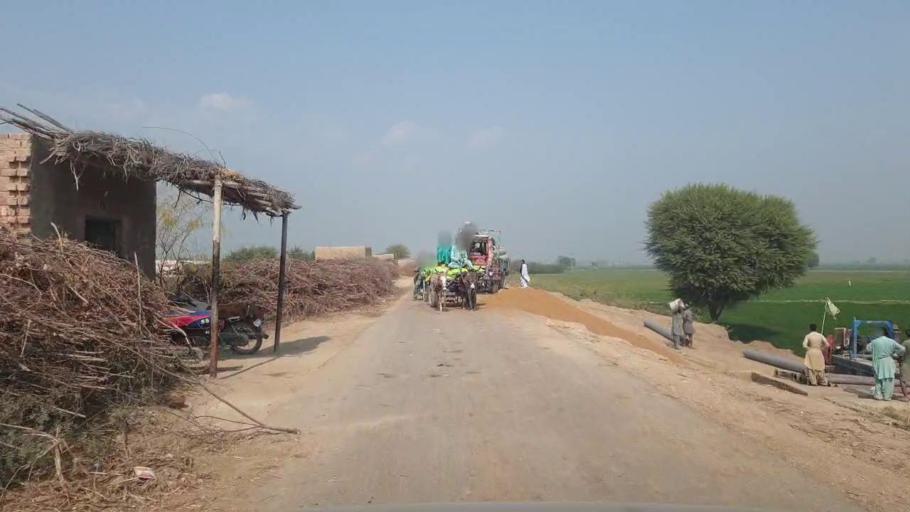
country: PK
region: Sindh
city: Hala
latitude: 25.7885
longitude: 68.4003
